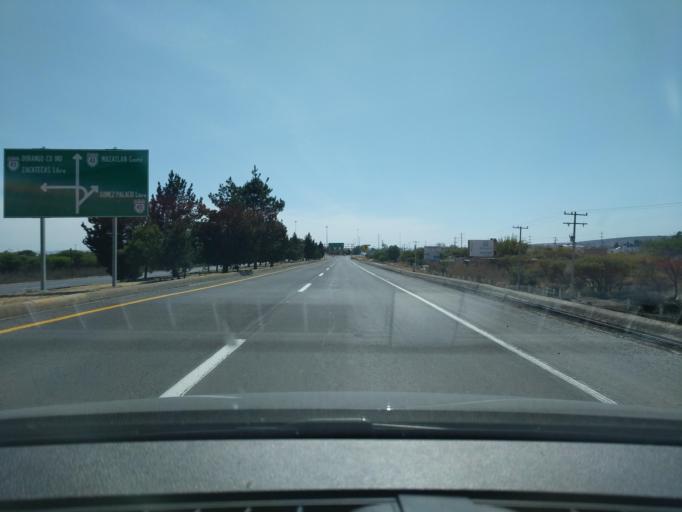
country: MX
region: Durango
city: Victoria de Durango
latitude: 24.0994
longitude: -104.5693
